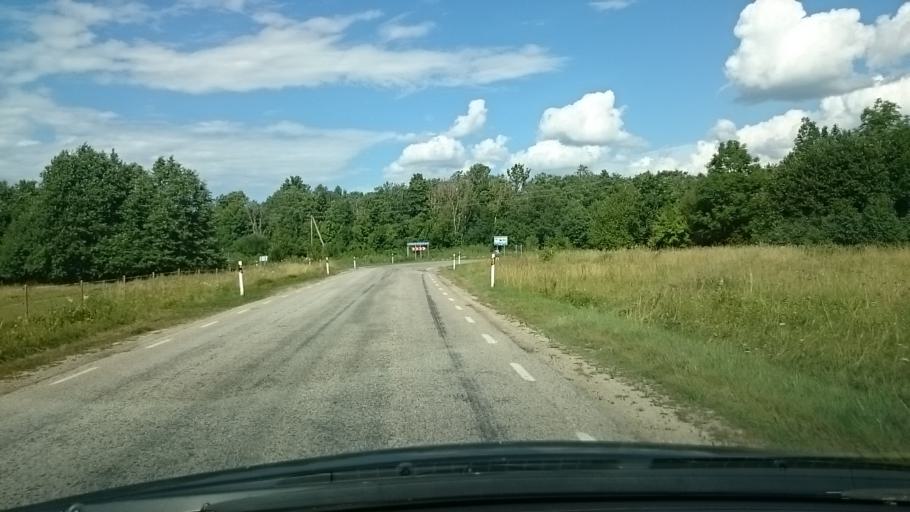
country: EE
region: Laeaene
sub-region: Haapsalu linn
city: Haapsalu
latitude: 59.1271
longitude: 23.5427
